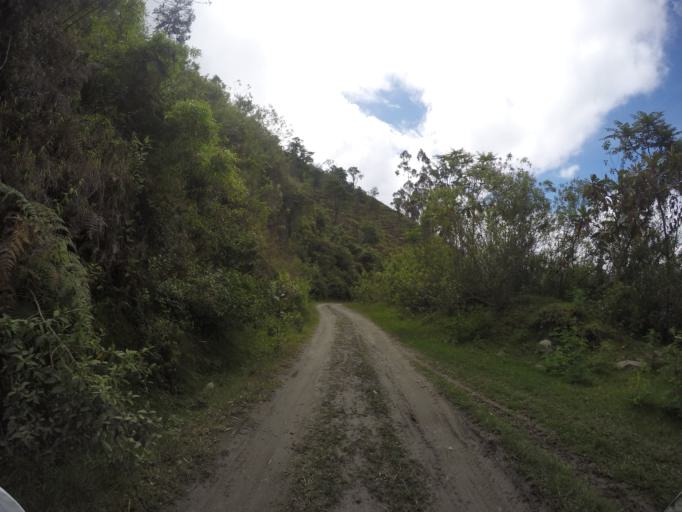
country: CO
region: Tolima
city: Cajamarca
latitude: 4.5330
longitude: -75.4323
